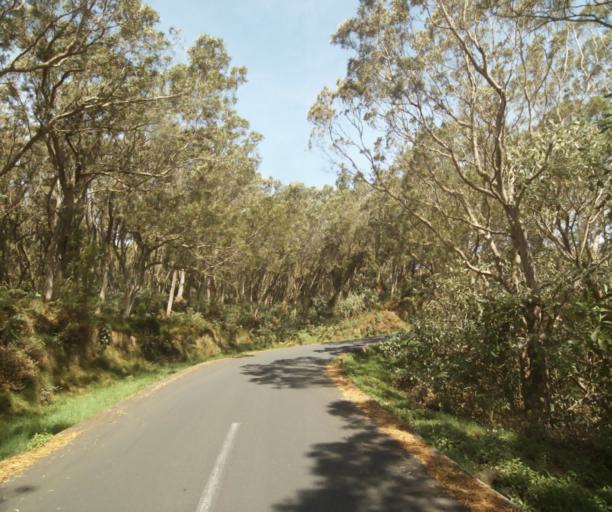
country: RE
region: Reunion
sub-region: Reunion
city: Trois-Bassins
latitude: -21.0581
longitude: 55.3642
